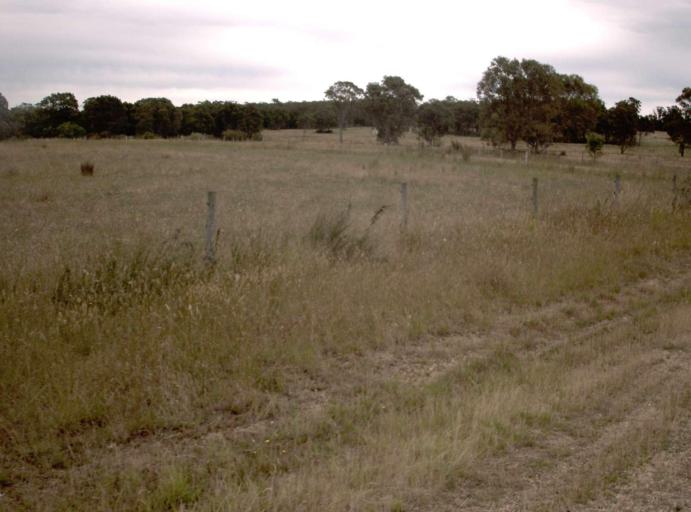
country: AU
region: Victoria
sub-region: East Gippsland
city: Bairnsdale
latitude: -37.9408
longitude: 147.5289
